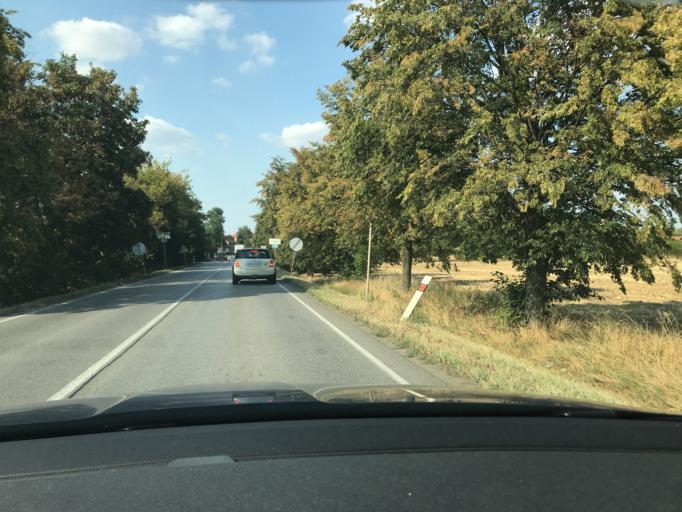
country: CZ
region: Central Bohemia
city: Velke Prilepy
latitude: 50.1872
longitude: 14.3210
